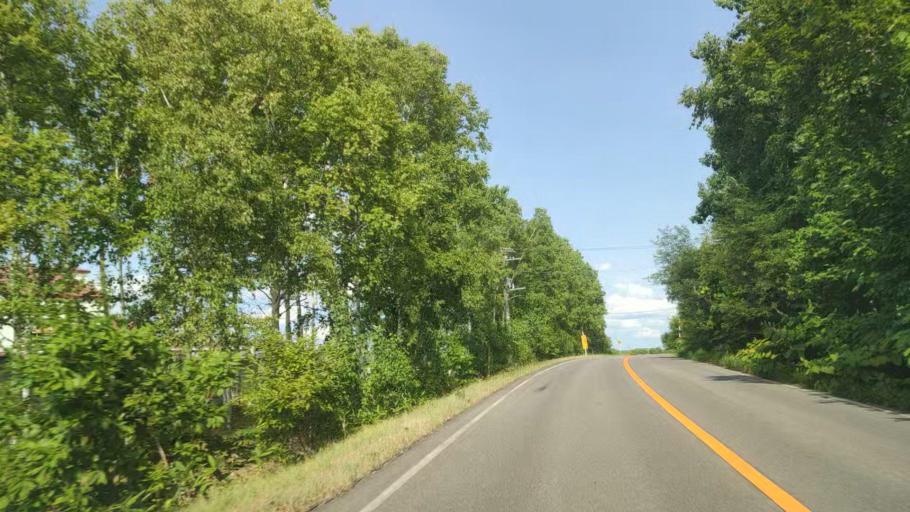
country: JP
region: Hokkaido
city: Nayoro
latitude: 44.2813
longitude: 142.4255
